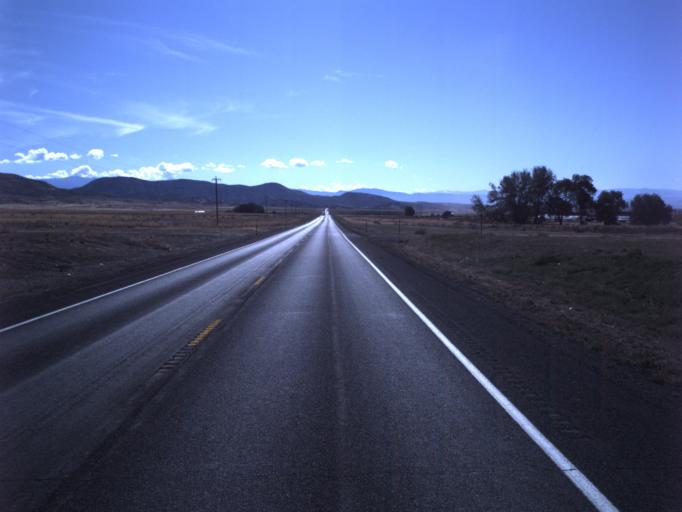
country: US
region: Utah
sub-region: Sanpete County
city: Gunnison
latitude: 39.2693
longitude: -111.8713
